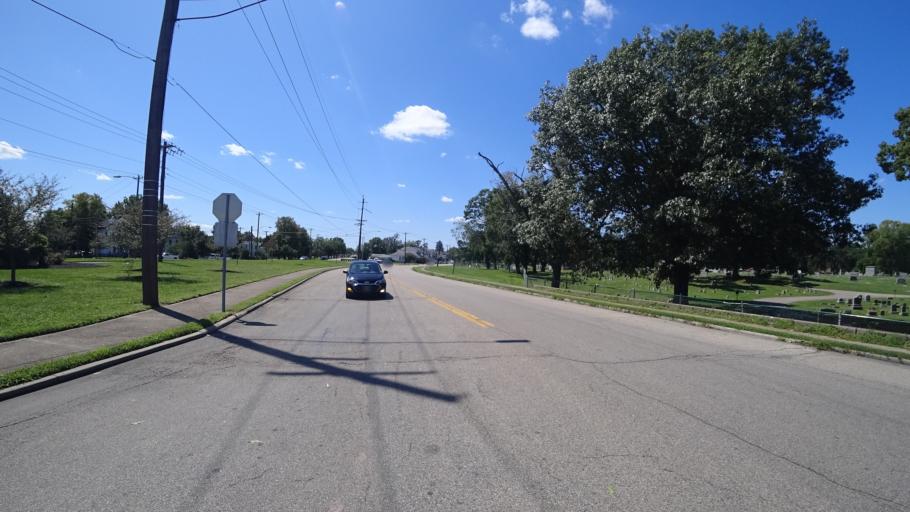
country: US
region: Ohio
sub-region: Butler County
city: Hamilton
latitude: 39.4021
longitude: -84.5410
